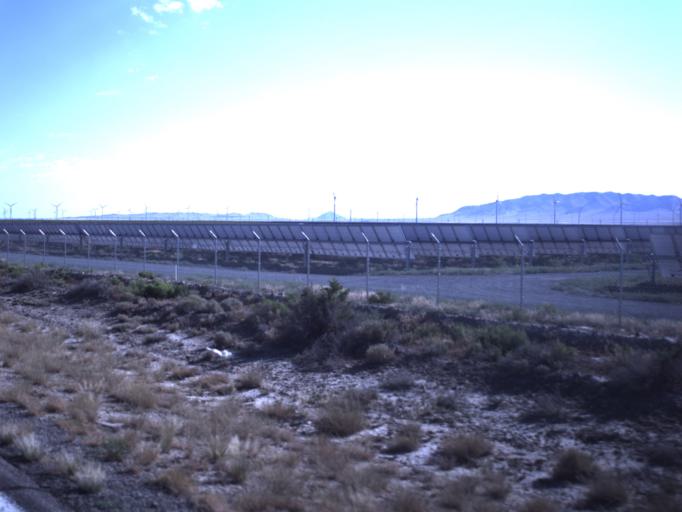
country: US
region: Utah
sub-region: Beaver County
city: Milford
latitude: 38.5107
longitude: -112.9911
